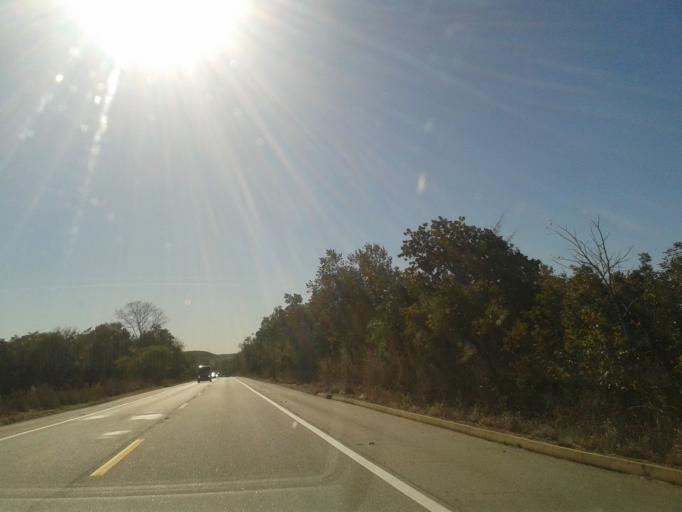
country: BR
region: Goias
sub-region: Itapirapua
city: Itapirapua
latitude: -15.3215
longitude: -50.4354
